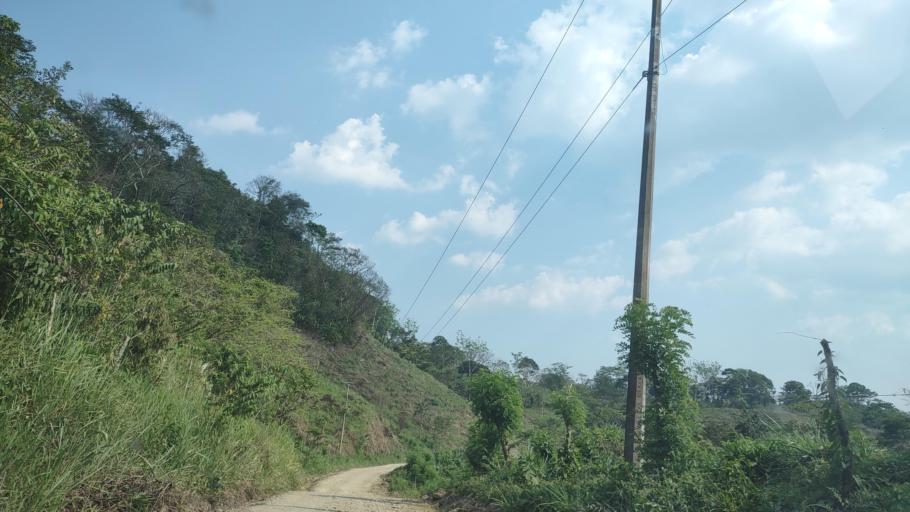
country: MX
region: Chiapas
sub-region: Tecpatan
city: Raudales Malpaso
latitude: 17.3196
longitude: -93.7414
